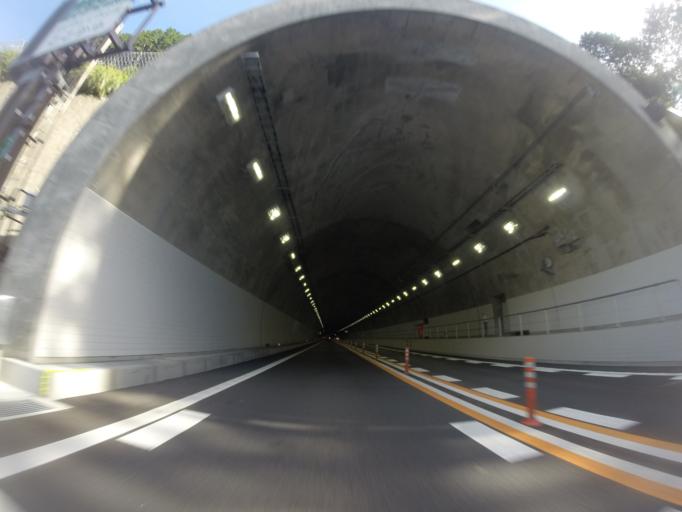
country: JP
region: Shizuoka
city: Fujinomiya
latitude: 35.1546
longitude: 138.4543
